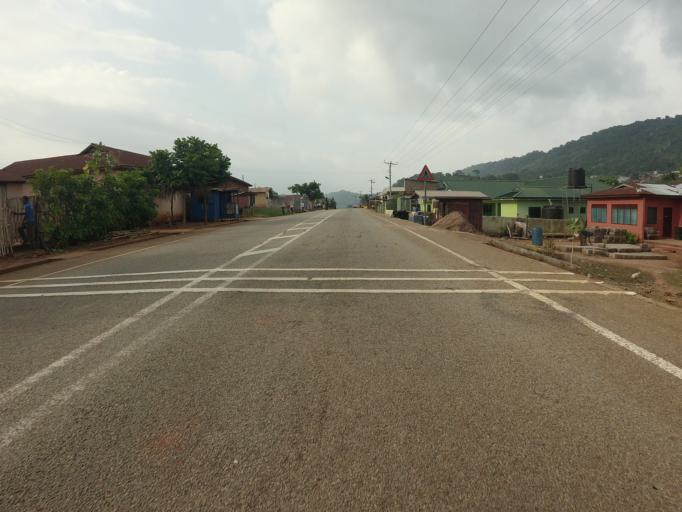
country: GH
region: Volta
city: Ho
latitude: 6.6665
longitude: 0.4747
